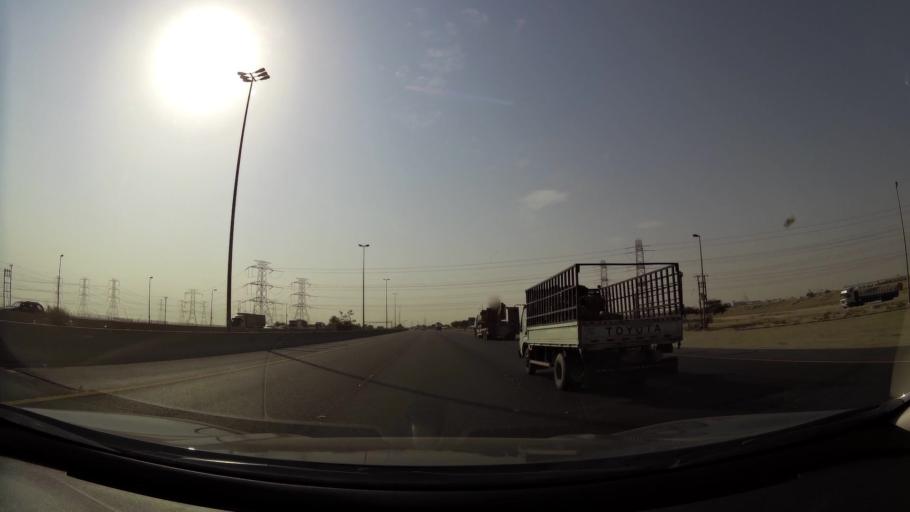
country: KW
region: Al Ahmadi
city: Al Ahmadi
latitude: 29.0061
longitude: 48.0949
